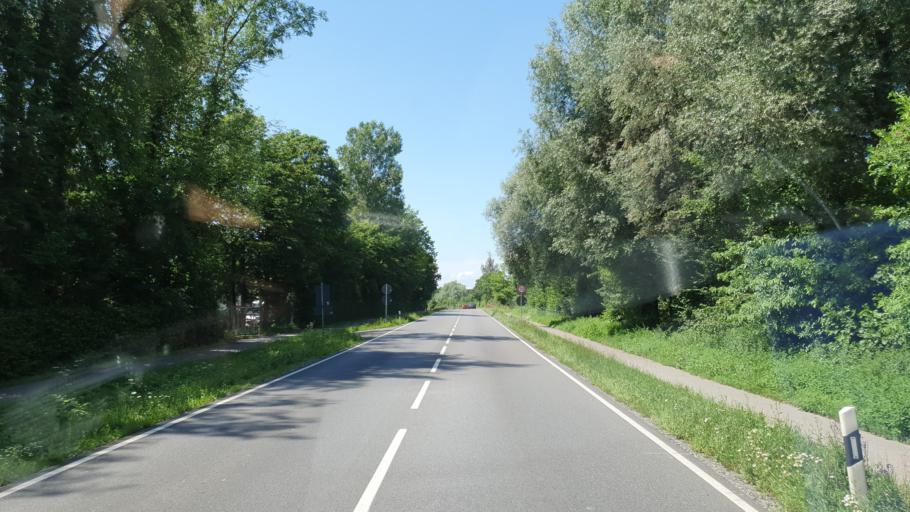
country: DE
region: Baden-Wuerttemberg
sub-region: Tuebingen Region
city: Immenstaad am Bodensee
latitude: 47.6713
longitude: 9.3910
